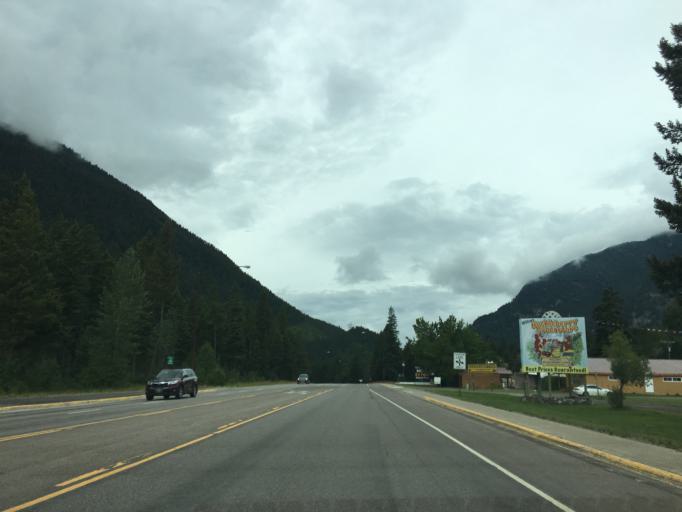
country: US
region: Montana
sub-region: Flathead County
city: Columbia Falls
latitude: 48.3857
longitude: -114.0701
